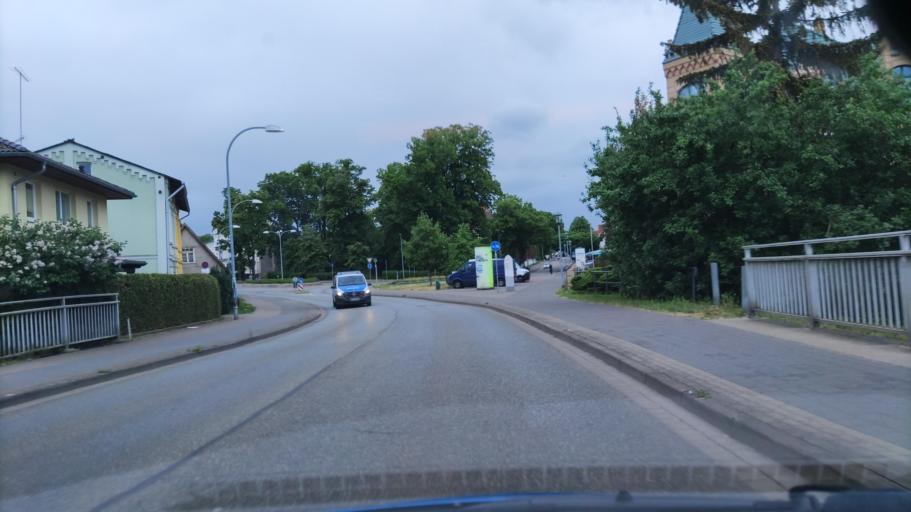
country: DE
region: Mecklenburg-Vorpommern
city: Parchim
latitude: 53.4294
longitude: 11.8379
